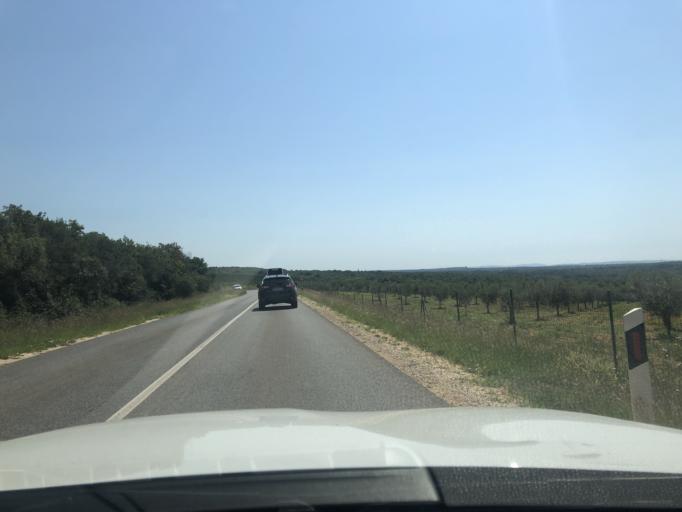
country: HR
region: Istarska
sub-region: Grad Rovinj
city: Rovinj
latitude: 45.0462
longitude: 13.7455
